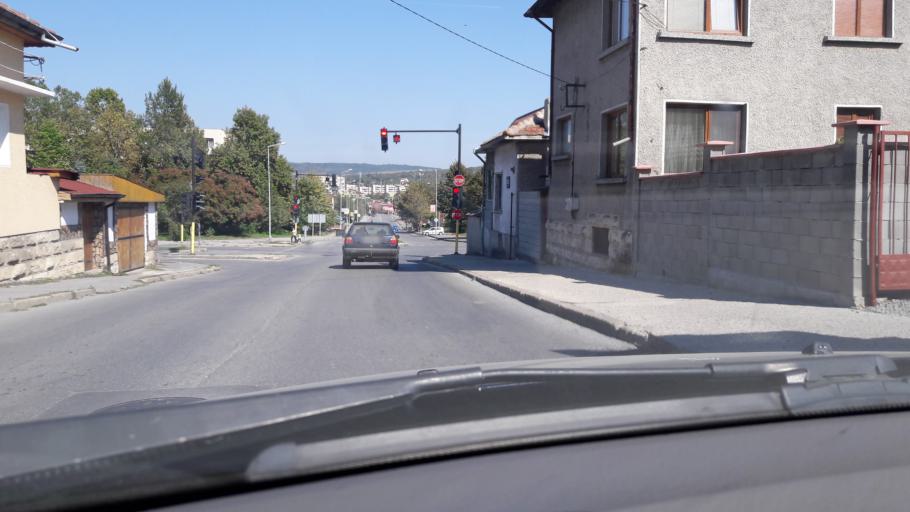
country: BG
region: Razgrad
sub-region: Obshtina Razgrad
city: Razgrad
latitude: 43.5259
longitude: 26.5156
